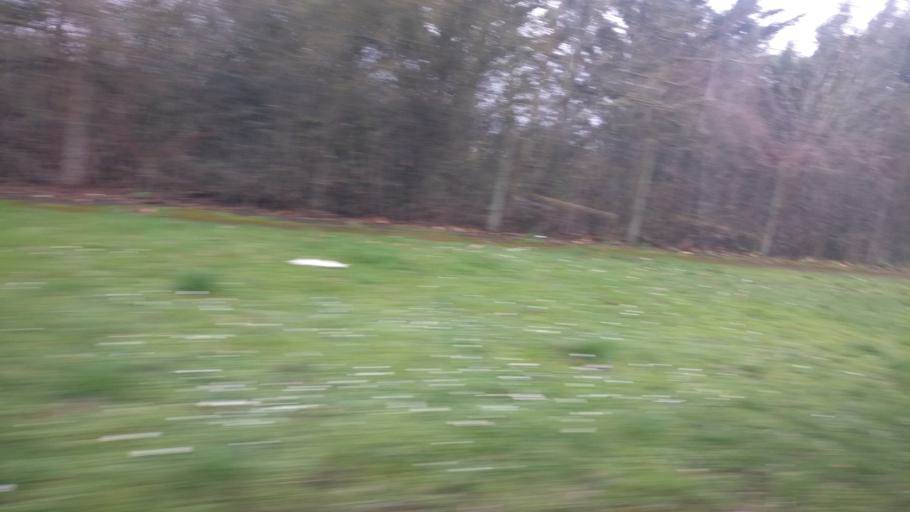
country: GB
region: England
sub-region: Surrey
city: Chertsey
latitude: 51.4051
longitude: -0.5058
